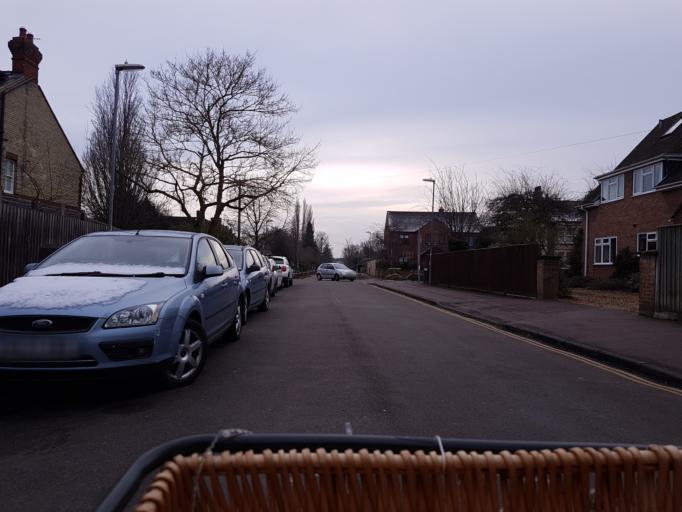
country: GB
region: England
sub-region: Cambridgeshire
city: Cambridge
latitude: 52.1856
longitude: 0.1447
